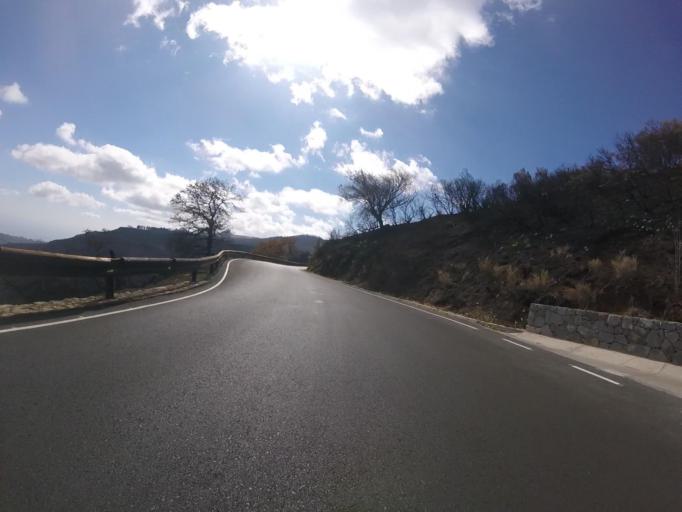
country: ES
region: Canary Islands
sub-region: Provincia de Las Palmas
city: Tejeda
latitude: 27.9967
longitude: -15.5952
